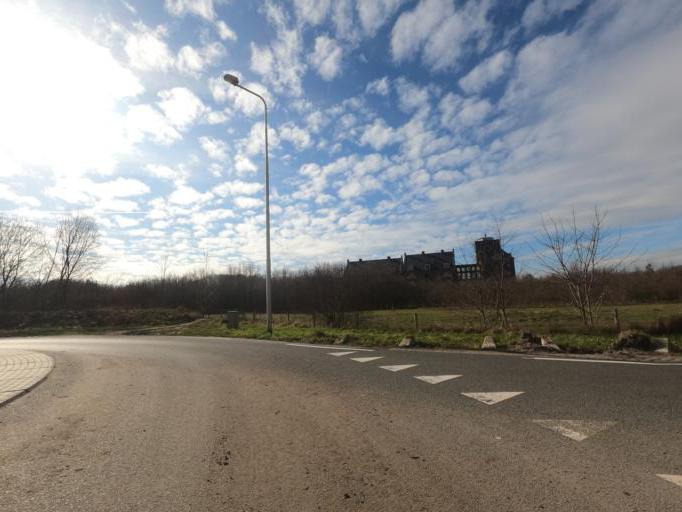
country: NL
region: Gelderland
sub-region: Gemeente Ermelo
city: Horst
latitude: 52.3244
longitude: 5.5799
